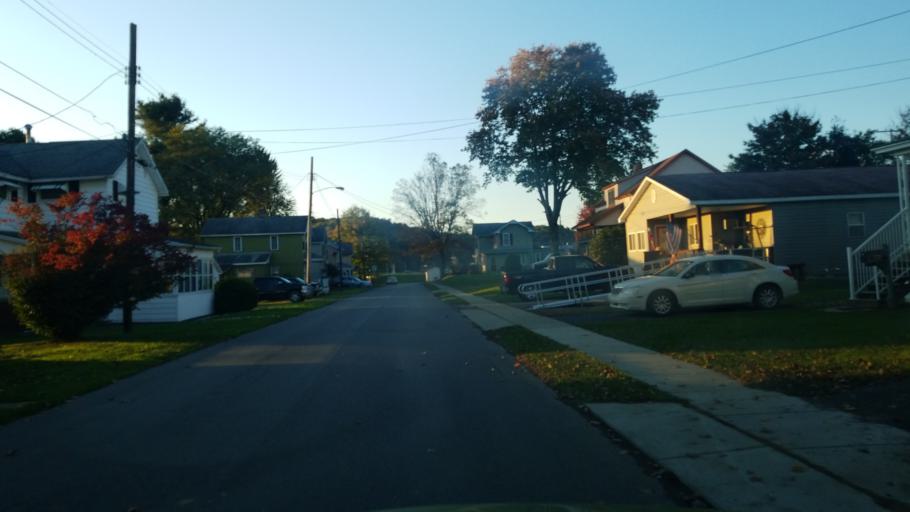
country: US
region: Pennsylvania
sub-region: Jefferson County
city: Reynoldsville
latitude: 41.0911
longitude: -78.8872
